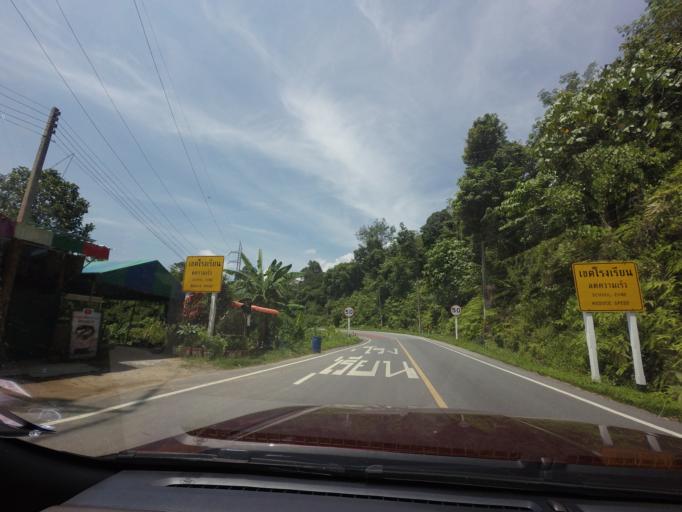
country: TH
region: Yala
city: Betong
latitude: 5.9173
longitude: 101.1749
